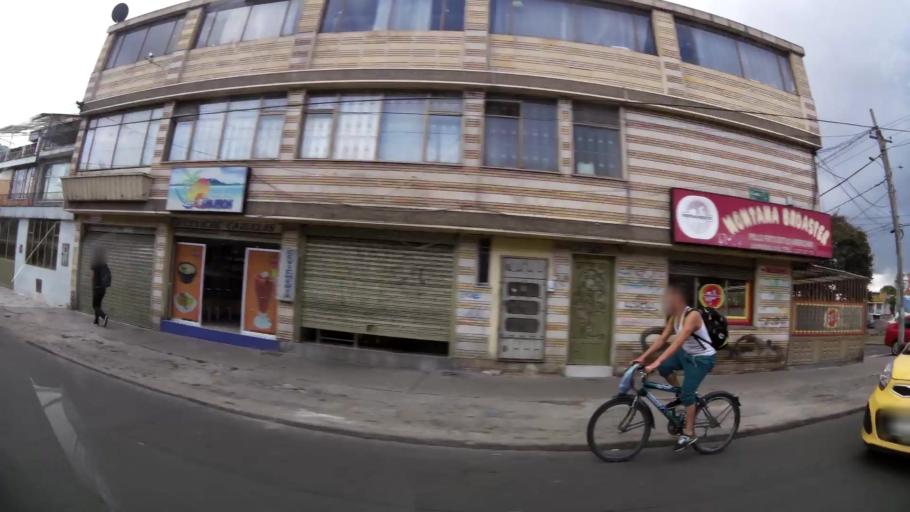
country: CO
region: Bogota D.C.
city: Bogota
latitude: 4.5974
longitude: -74.1011
